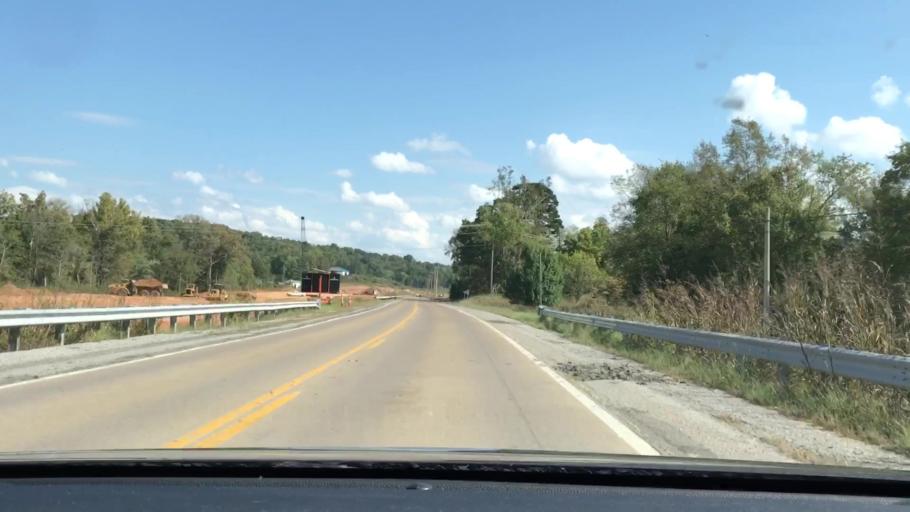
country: US
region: Kentucky
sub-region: Trigg County
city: Cadiz
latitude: 36.8002
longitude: -87.9412
